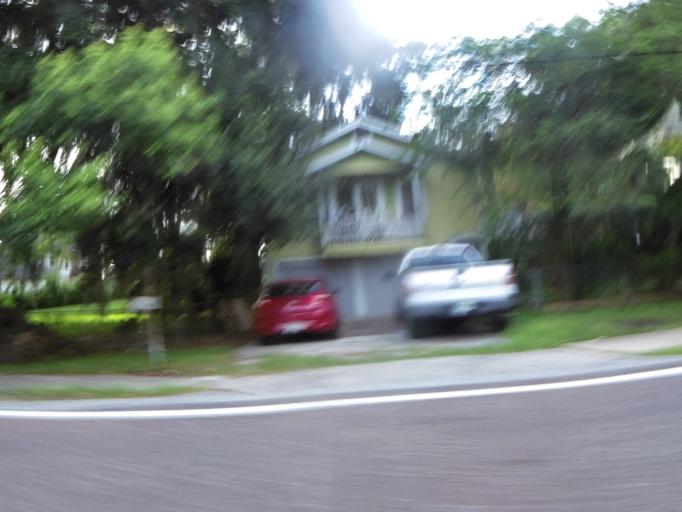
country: US
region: Florida
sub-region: Duval County
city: Jacksonville
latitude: 30.4164
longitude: -81.7063
